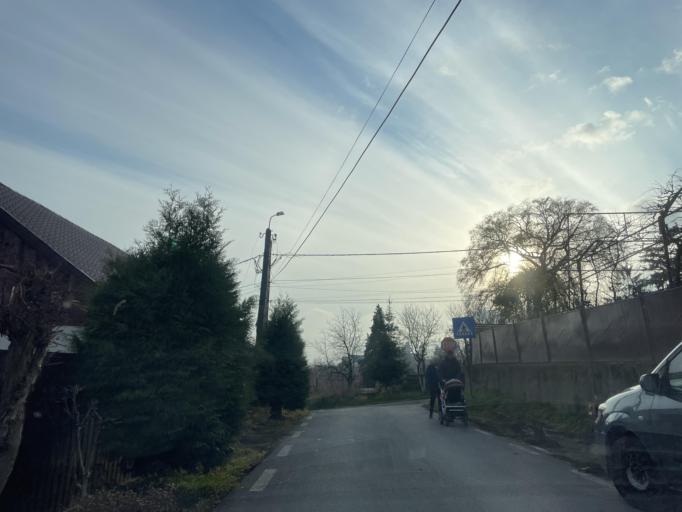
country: RO
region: Mures
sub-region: Municipiul Reghin
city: Reghin
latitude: 46.7810
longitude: 24.6925
